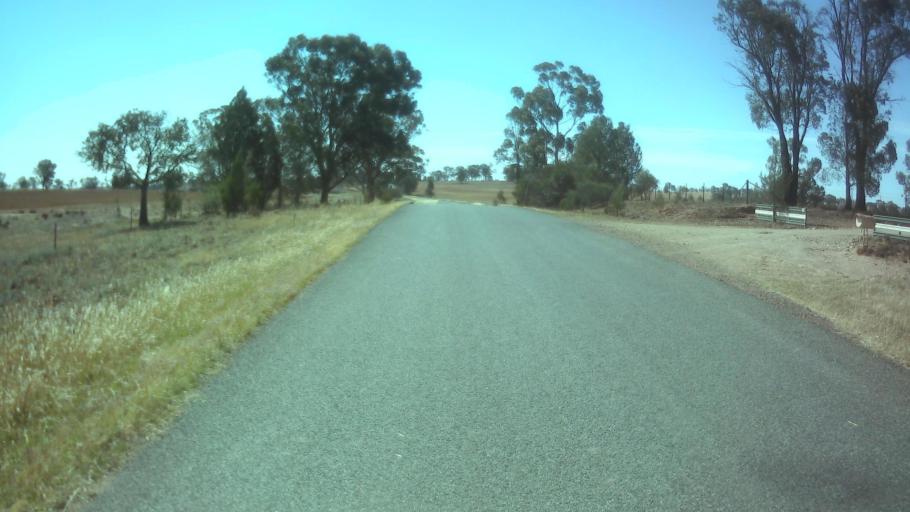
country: AU
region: New South Wales
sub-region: Weddin
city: Grenfell
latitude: -33.7623
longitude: 147.8621
